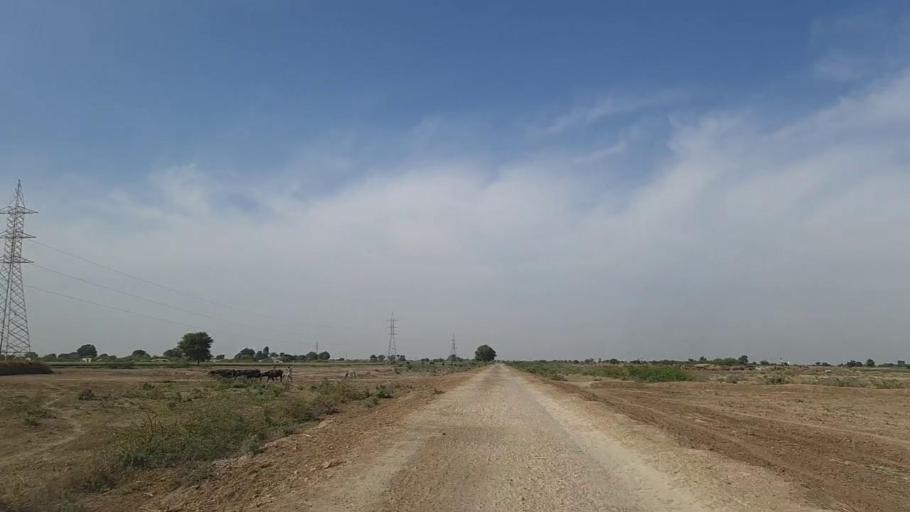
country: PK
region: Sindh
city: Samaro
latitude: 25.2182
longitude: 69.4517
